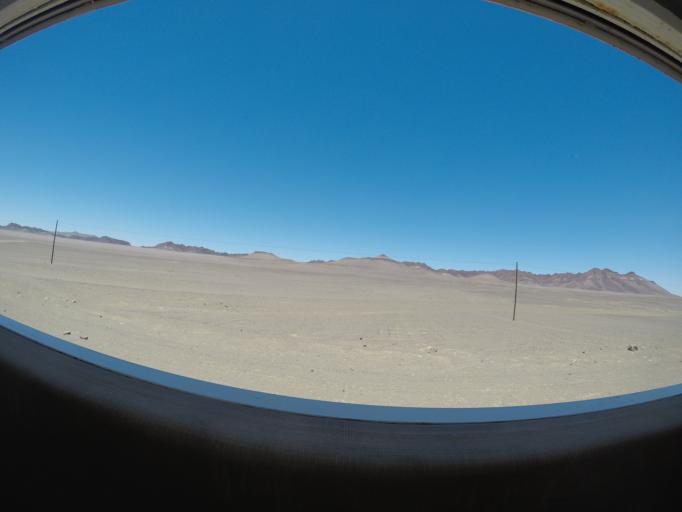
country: ZA
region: Northern Cape
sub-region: Namakwa District Municipality
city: Port Nolloth
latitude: -28.5907
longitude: 17.4828
